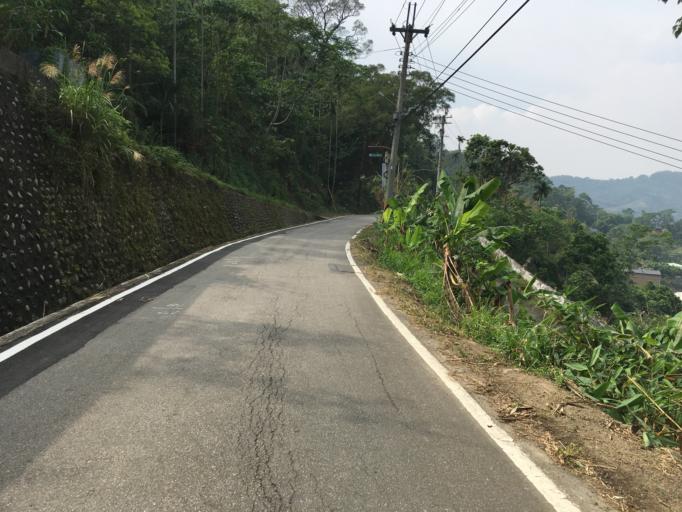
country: TW
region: Taiwan
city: Fengyuan
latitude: 24.1861
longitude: 120.7537
